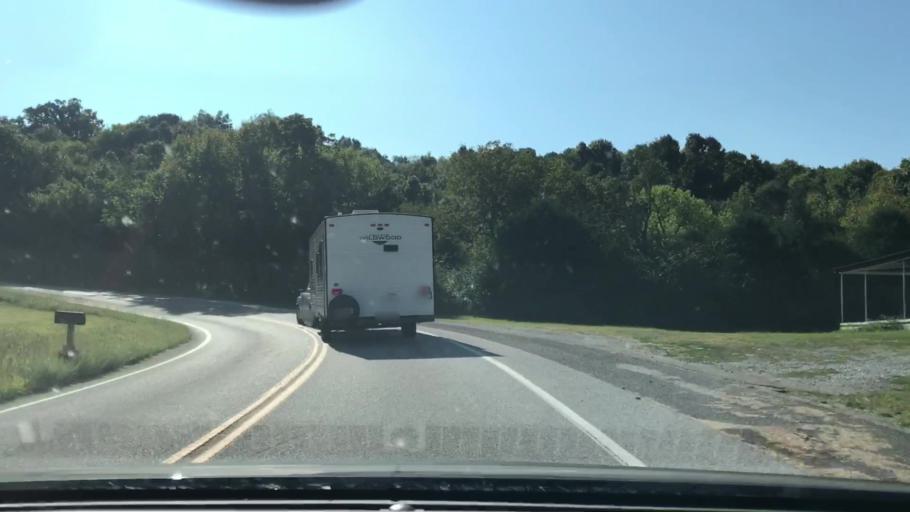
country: US
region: Tennessee
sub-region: Smith County
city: Carthage
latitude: 36.3451
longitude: -85.8586
